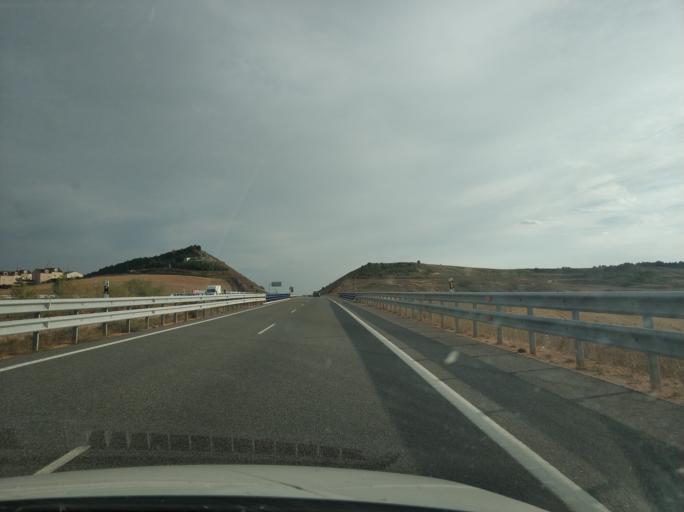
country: ES
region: Castille and Leon
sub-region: Provincia de Burgos
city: Quintanaortuno
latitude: 42.4545
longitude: -3.6898
